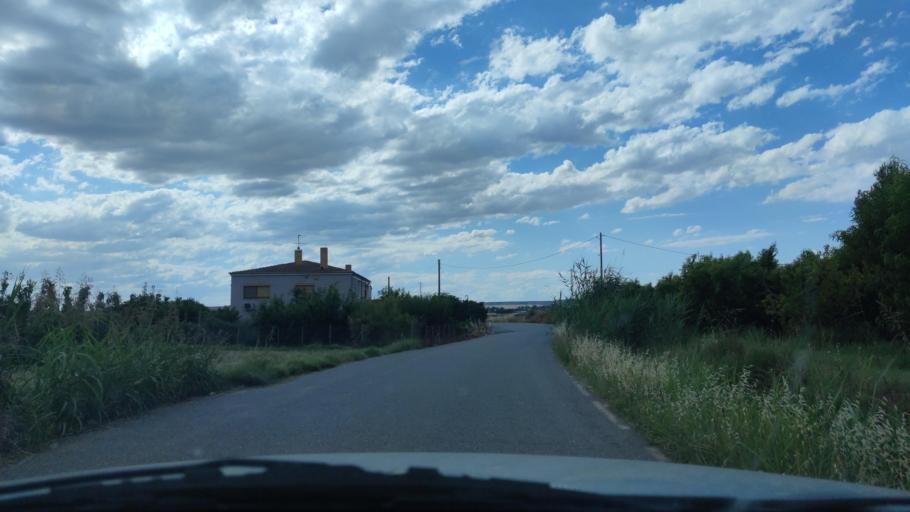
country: ES
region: Catalonia
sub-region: Provincia de Lleida
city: Lleida
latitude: 41.5969
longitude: 0.5695
